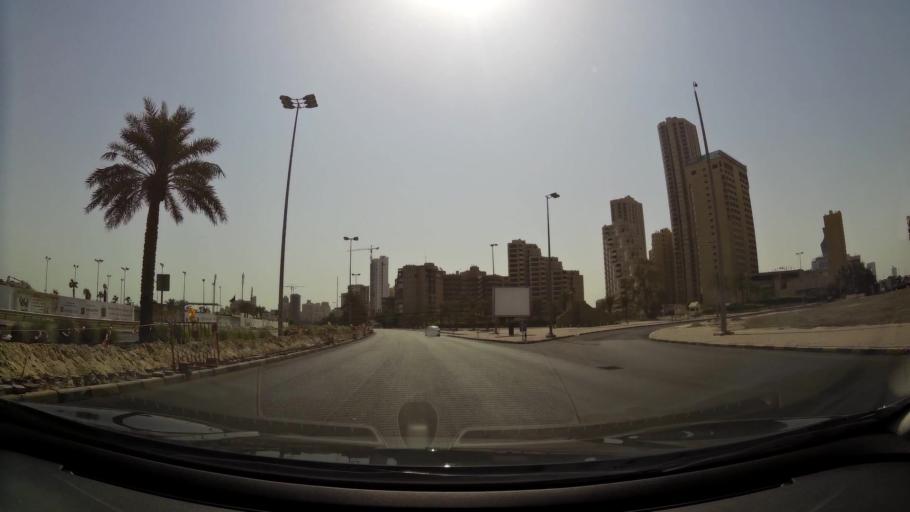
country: KW
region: Al Asimah
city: Ad Dasmah
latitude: 29.3795
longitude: 48.0031
